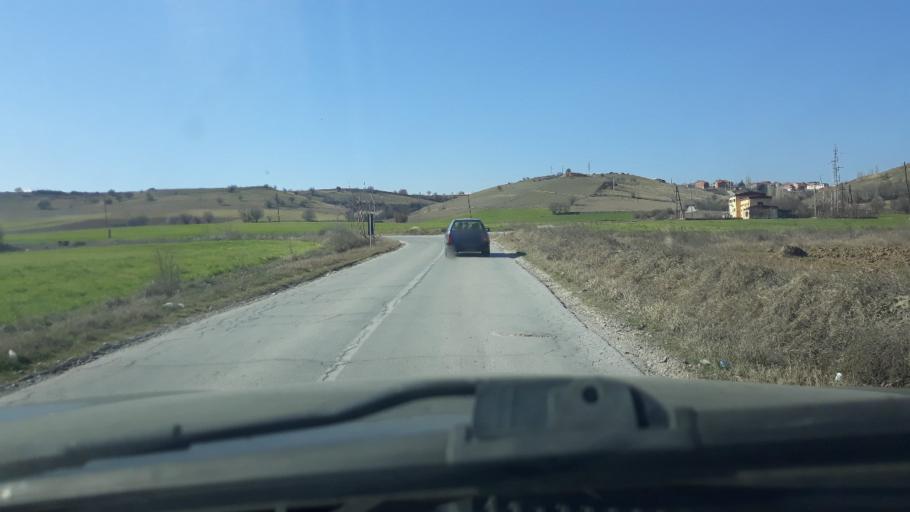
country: MK
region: Veles
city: Gorno Orizari
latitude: 41.6758
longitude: 21.7422
